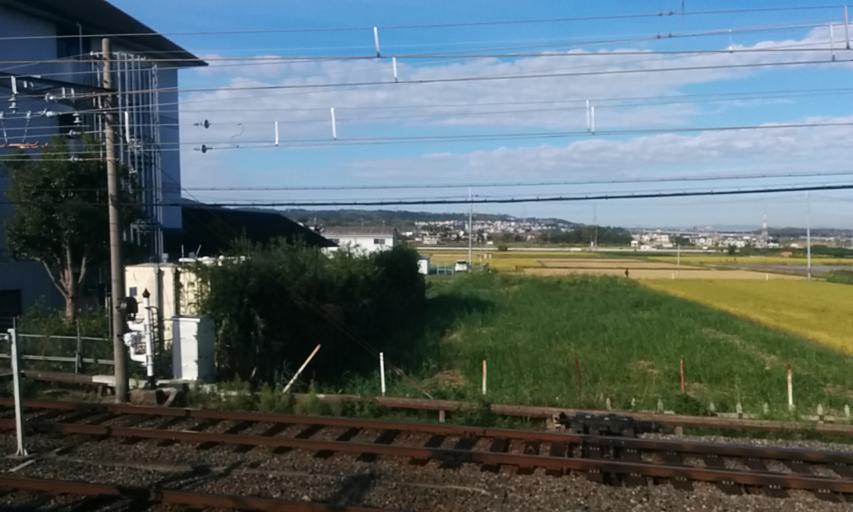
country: JP
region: Kyoto
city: Tanabe
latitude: 34.8252
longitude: 135.7736
